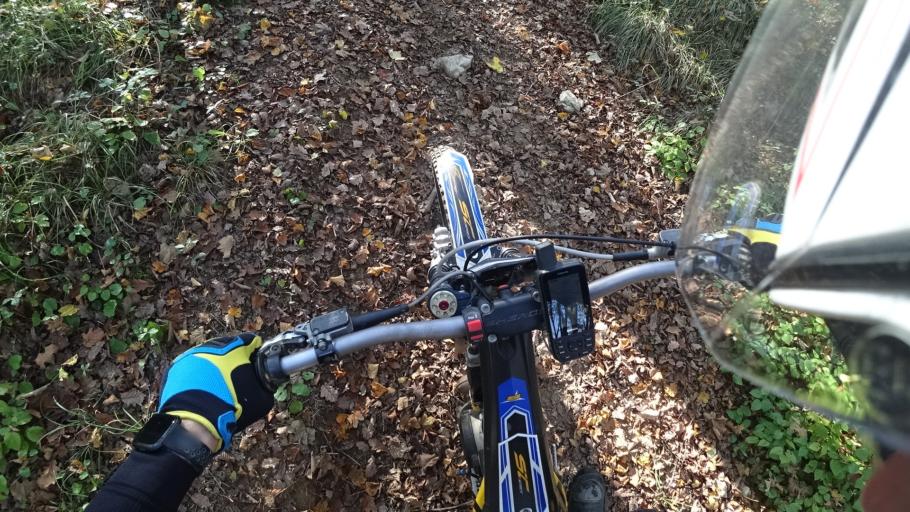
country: HR
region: Primorsko-Goranska
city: Matulji
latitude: 45.3894
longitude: 14.2975
